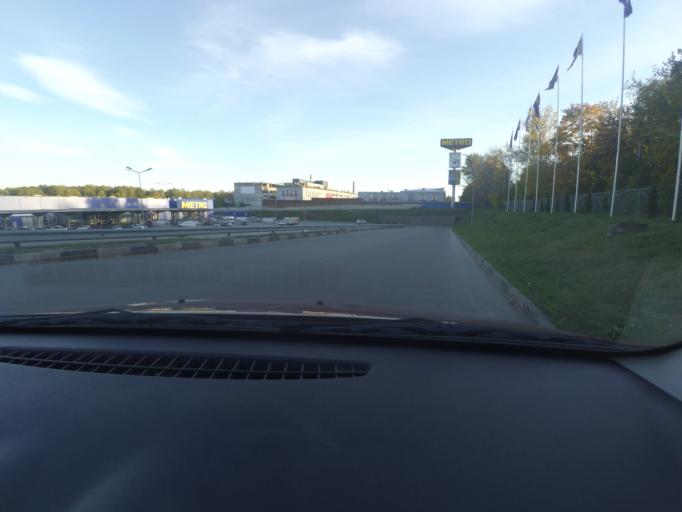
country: RU
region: Nizjnij Novgorod
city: Nizhniy Novgorod
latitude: 56.2878
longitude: 43.9953
